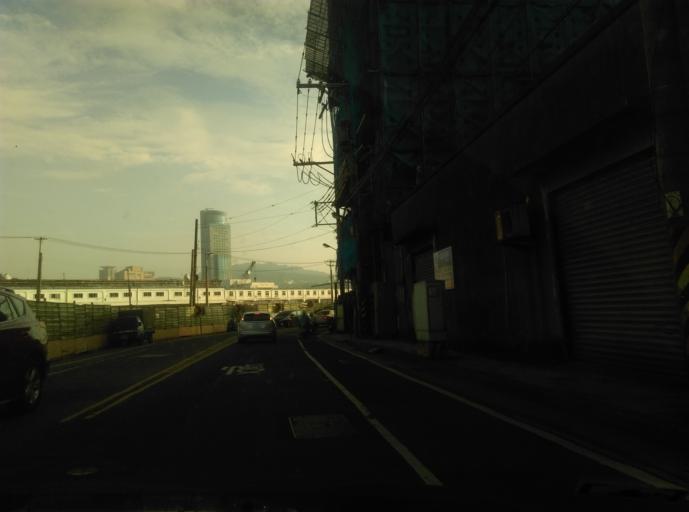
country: TW
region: Taiwan
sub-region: Keelung
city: Keelung
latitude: 25.1371
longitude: 121.7409
